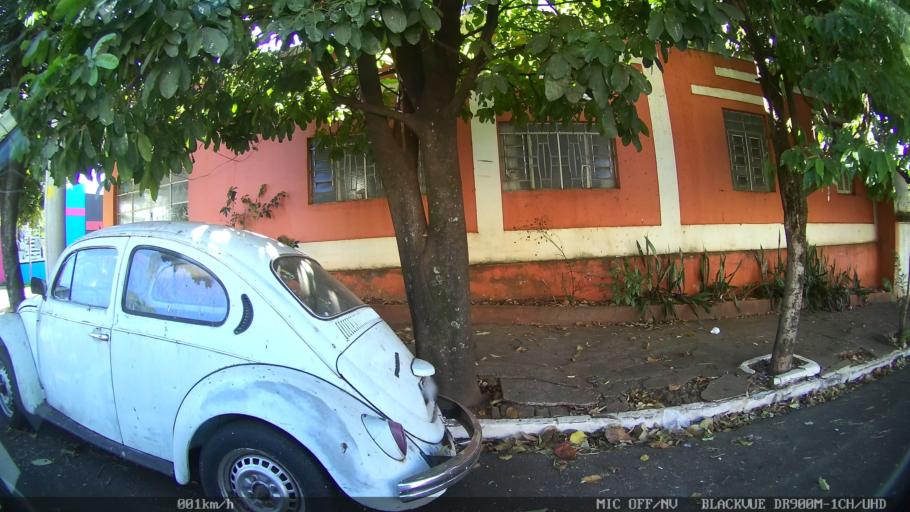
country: BR
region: Sao Paulo
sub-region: Olimpia
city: Olimpia
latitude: -20.7412
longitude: -48.9136
